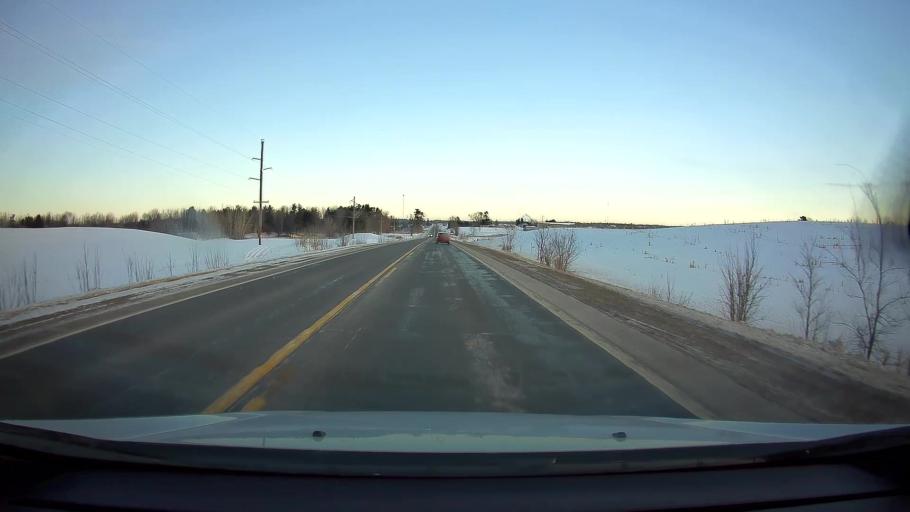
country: US
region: Wisconsin
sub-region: Barron County
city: Turtle Lake
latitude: 45.3742
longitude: -92.1668
